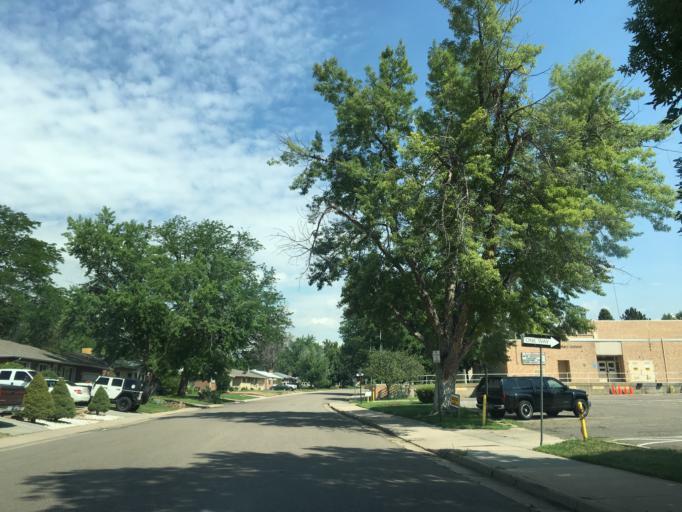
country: US
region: Colorado
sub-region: Arapahoe County
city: Sheridan
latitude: 39.6585
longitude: -105.0463
